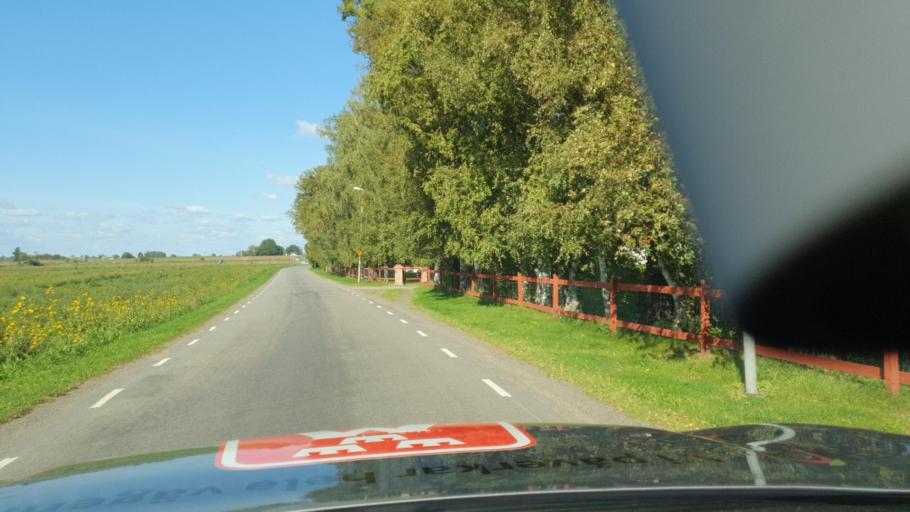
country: SE
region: Skane
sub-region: Kristianstads Kommun
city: Fjalkinge
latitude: 56.0123
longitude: 14.2487
